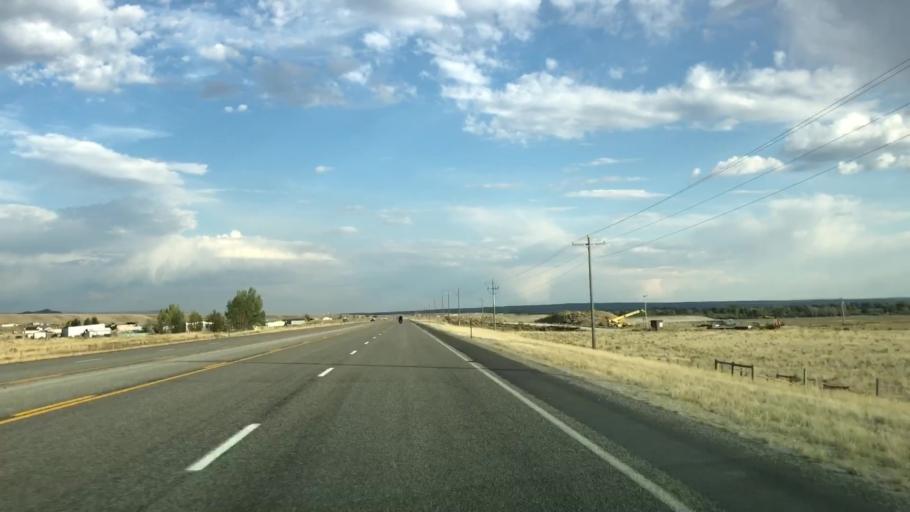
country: US
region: Wyoming
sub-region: Sublette County
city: Pinedale
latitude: 42.7730
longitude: -109.7562
